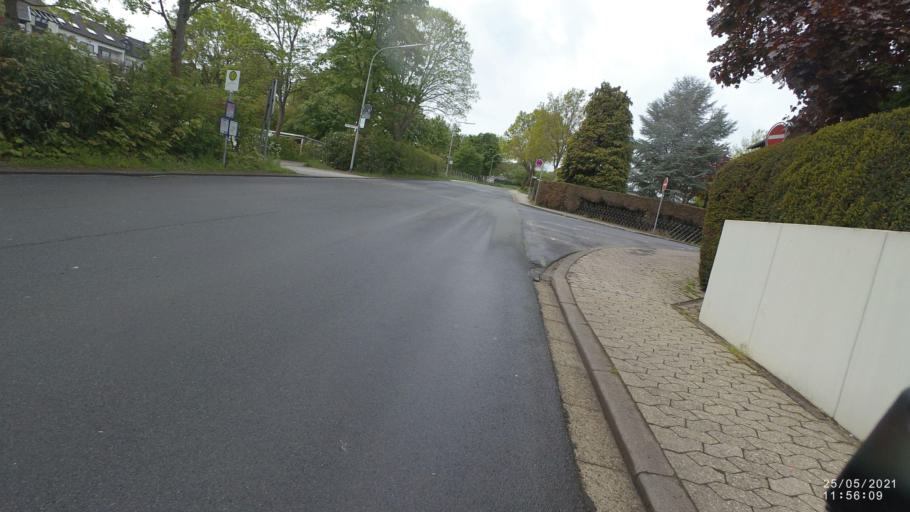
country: DE
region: Rheinland-Pfalz
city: Mayen
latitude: 50.3202
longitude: 7.2164
